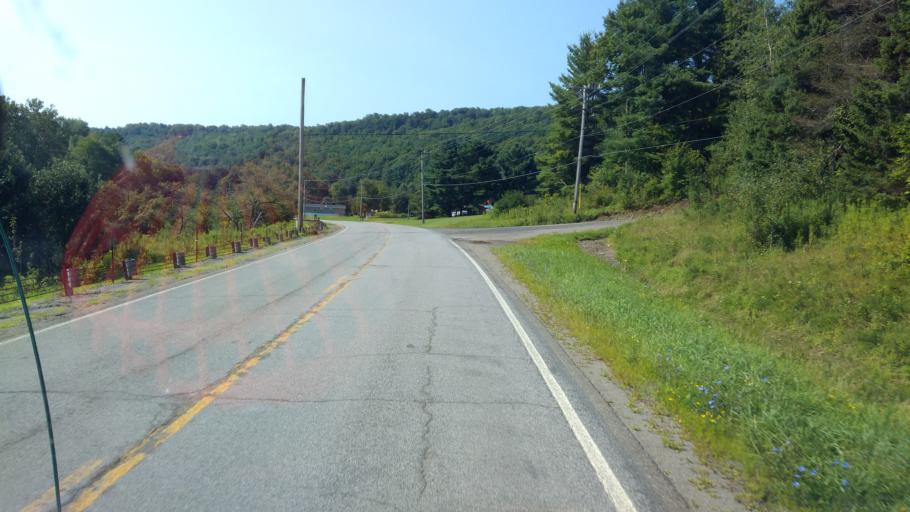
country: US
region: New York
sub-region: Allegany County
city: Bolivar
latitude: 42.1082
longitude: -78.1627
